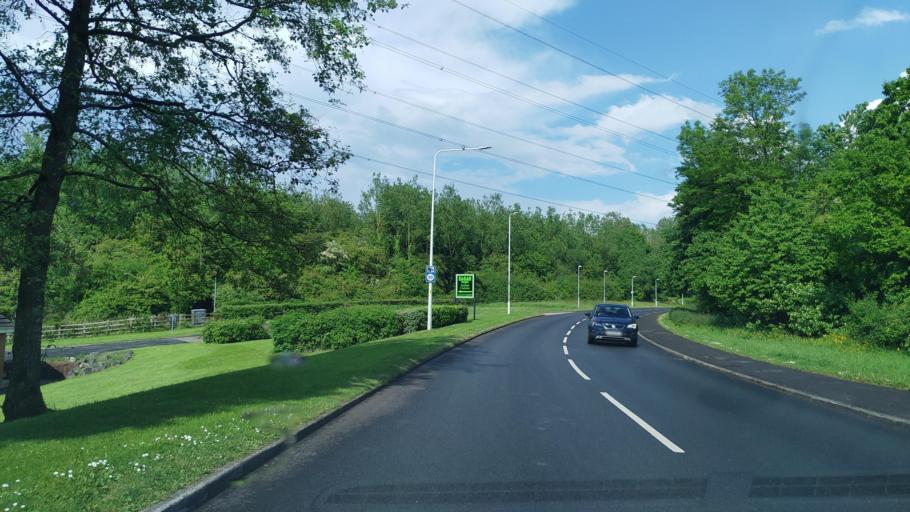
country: GB
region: England
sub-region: Lancashire
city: Clayton-le-Woods
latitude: 53.7170
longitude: -2.6381
